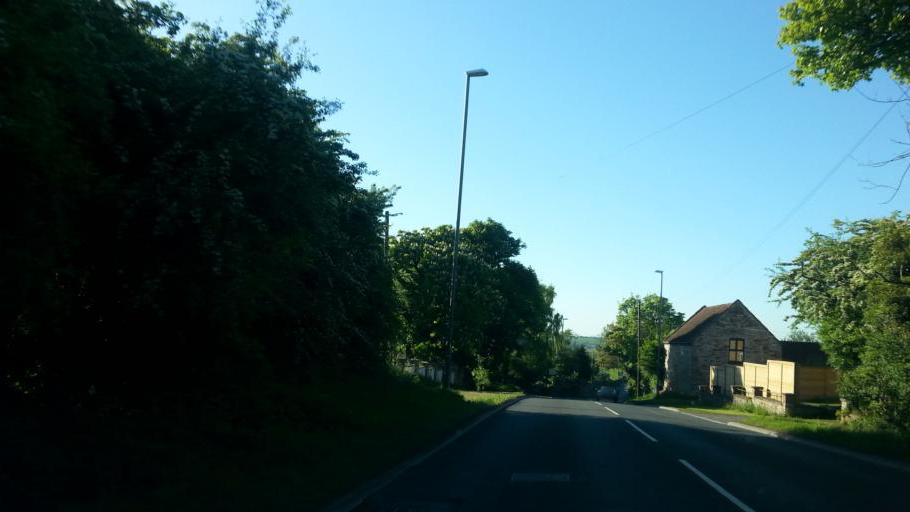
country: GB
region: England
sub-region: Bath and North East Somerset
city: Clutton
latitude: 51.3517
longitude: -2.5391
